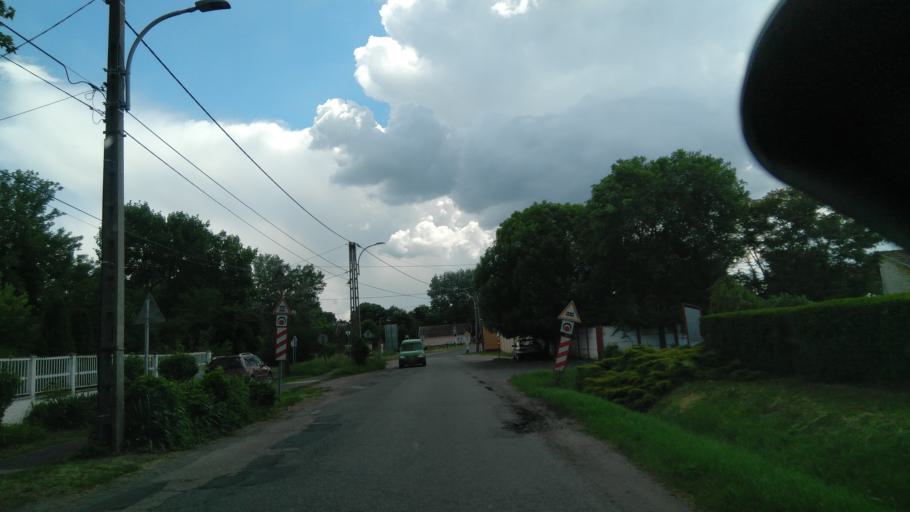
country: HU
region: Bekes
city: Gyula
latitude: 46.6578
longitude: 21.2695
